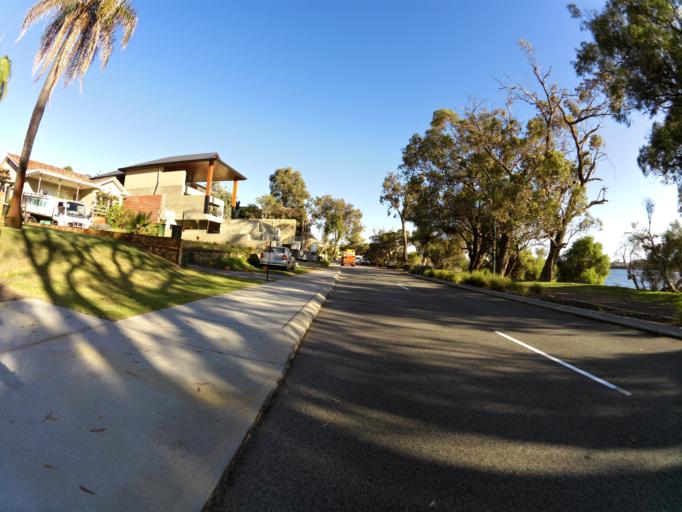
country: AU
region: Western Australia
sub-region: Melville
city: Mount Pleasant
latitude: -32.0345
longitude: 115.8539
